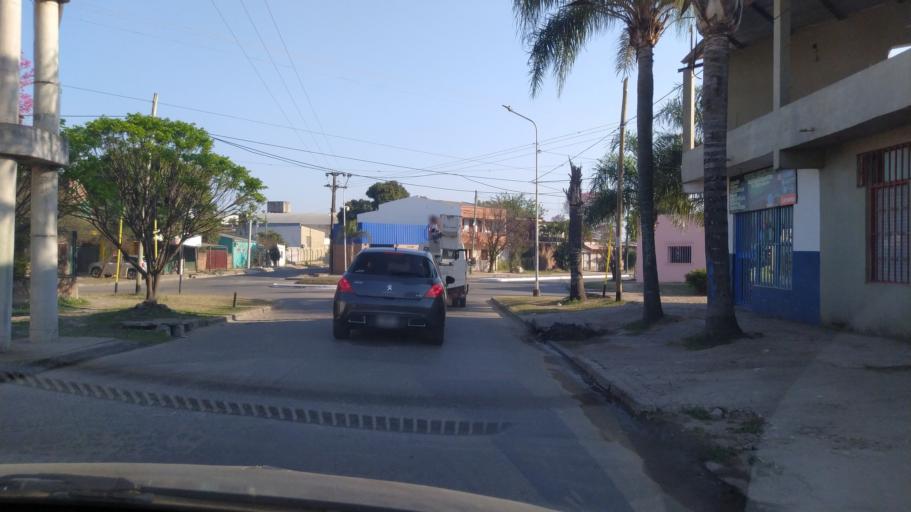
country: AR
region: Corrientes
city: Corrientes
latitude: -27.4925
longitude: -58.8169
